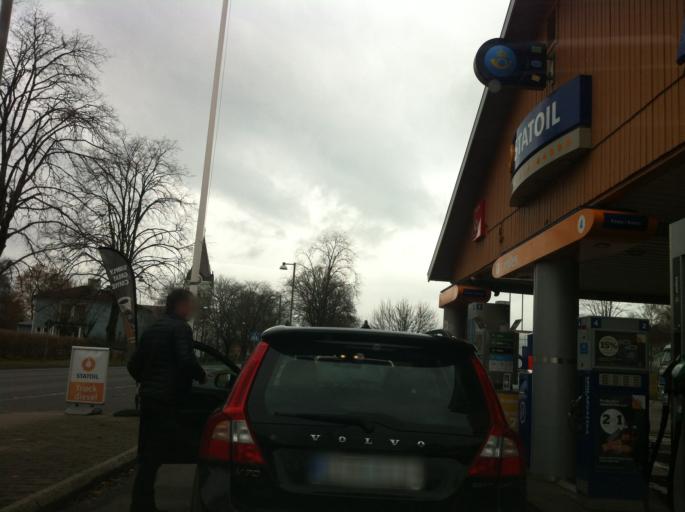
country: SE
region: Joenkoeping
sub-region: Savsjo Kommun
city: Vrigstad
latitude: 57.3640
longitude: 14.4965
